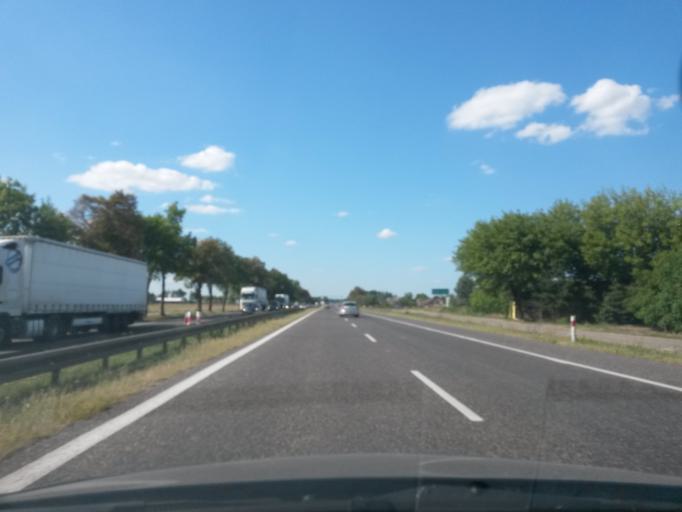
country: PL
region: Masovian Voivodeship
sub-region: Powiat plonski
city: Zaluski
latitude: 52.5442
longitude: 20.5062
